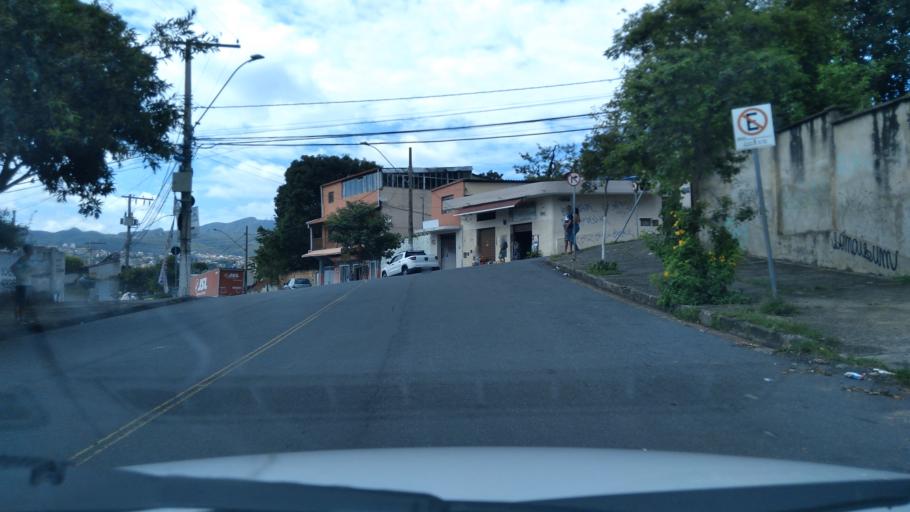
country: BR
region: Minas Gerais
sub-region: Belo Horizonte
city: Belo Horizonte
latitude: -19.8954
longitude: -43.8880
